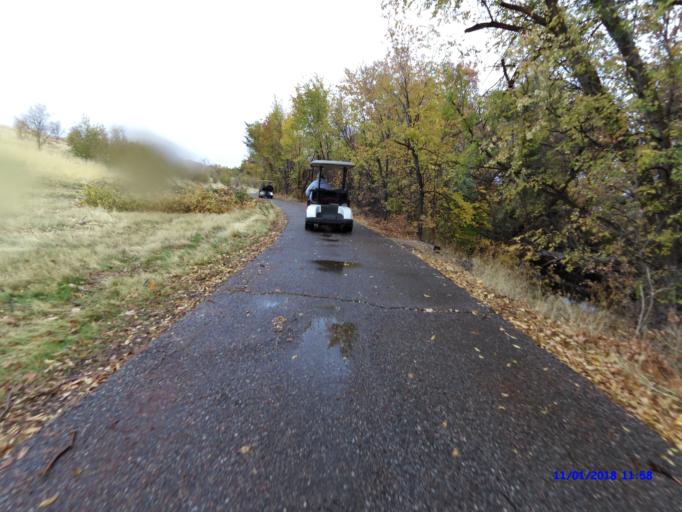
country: US
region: Utah
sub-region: Weber County
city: Ogden
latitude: 41.2350
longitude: -111.9993
